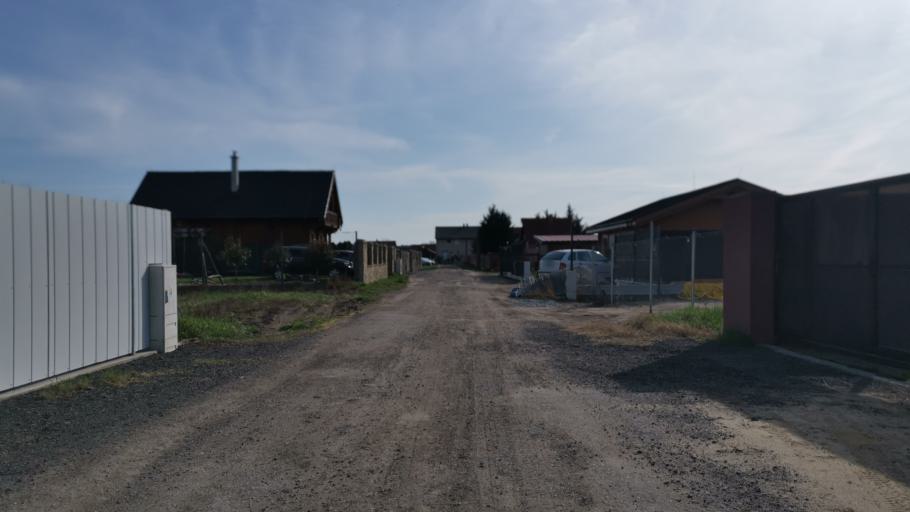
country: CZ
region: South Moravian
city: Tvrdonice
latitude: 48.7303
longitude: 17.0418
